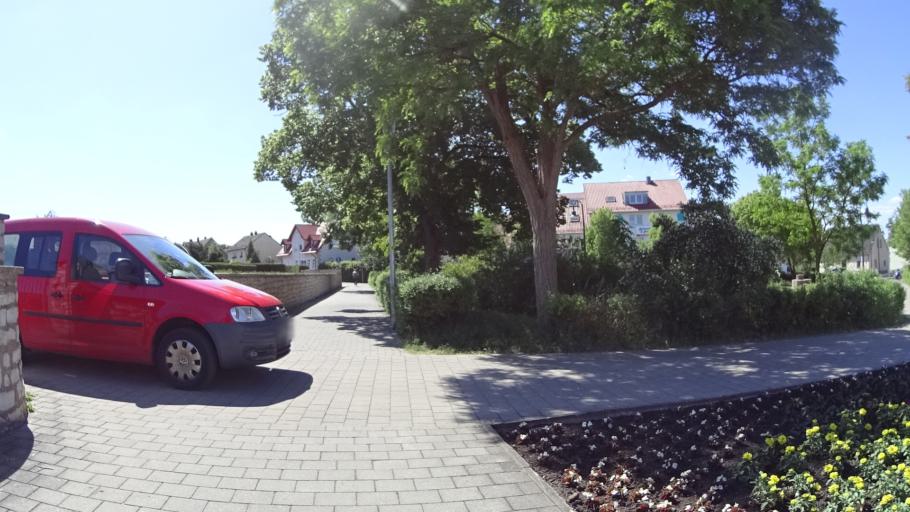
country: DE
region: Bavaria
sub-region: Regierungsbezirk Mittelfranken
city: Gunzenhausen
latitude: 49.1152
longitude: 10.7626
